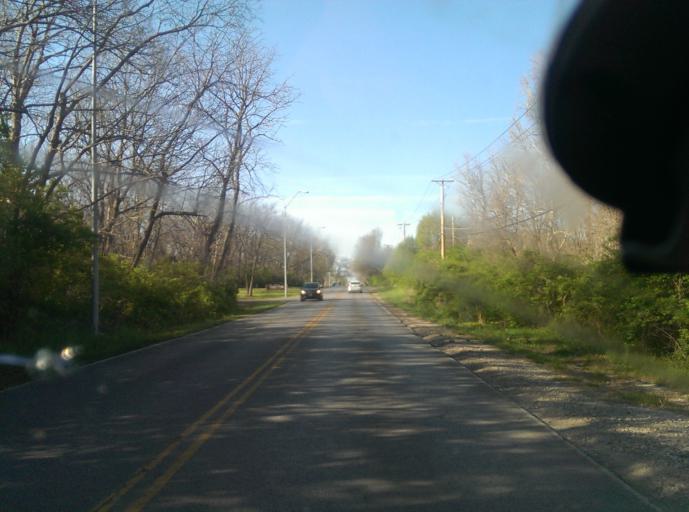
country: US
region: Missouri
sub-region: Jackson County
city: Grandview
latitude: 38.9078
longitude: -94.5848
